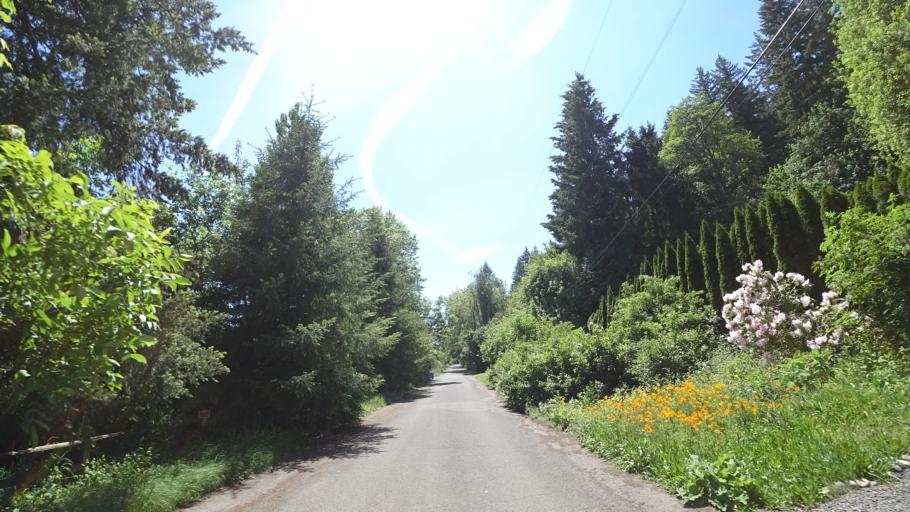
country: US
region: Oregon
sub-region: Clackamas County
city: Happy Valley
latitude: 45.4852
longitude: -122.4909
